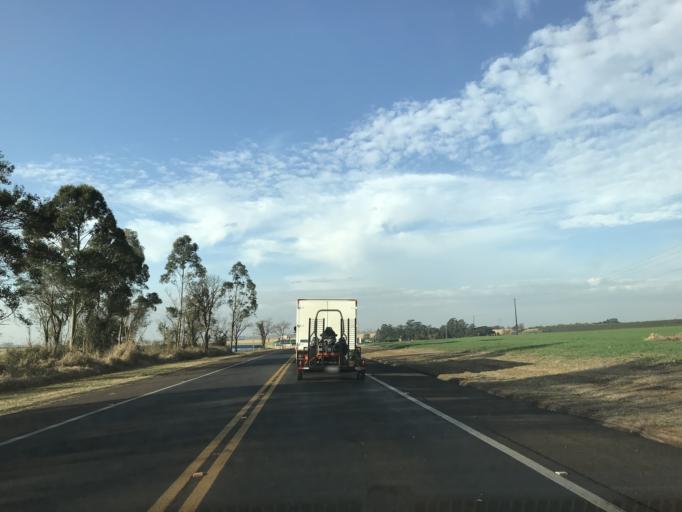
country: BR
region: Parana
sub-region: Cascavel
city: Cascavel
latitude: -25.0318
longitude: -53.5857
